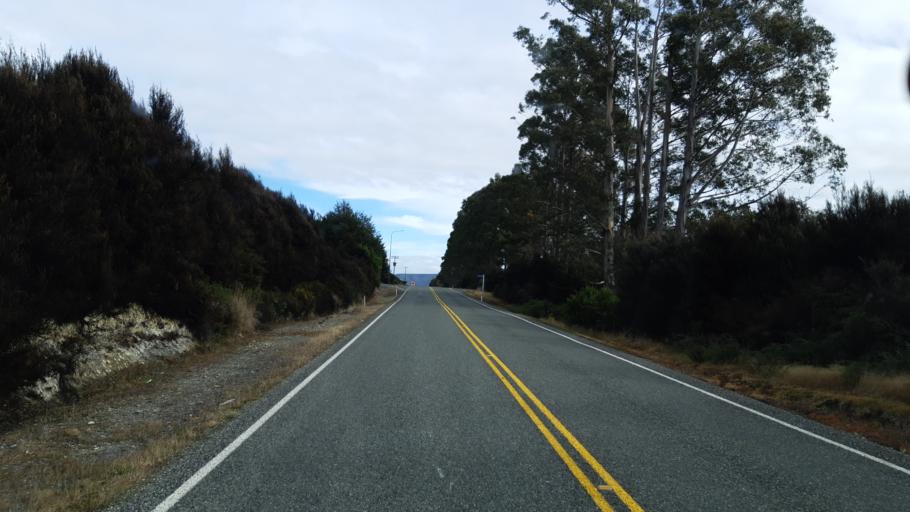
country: NZ
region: Tasman
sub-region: Tasman District
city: Wakefield
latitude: -41.7826
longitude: 172.9025
